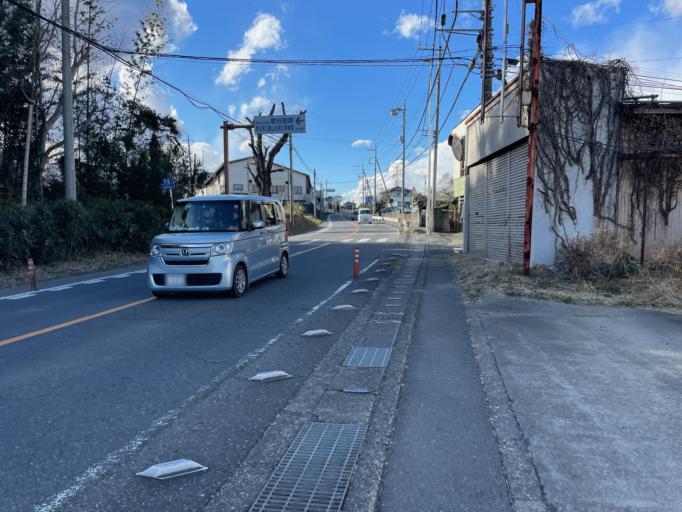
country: JP
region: Saitama
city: Ogawa
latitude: 36.0366
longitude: 139.3386
